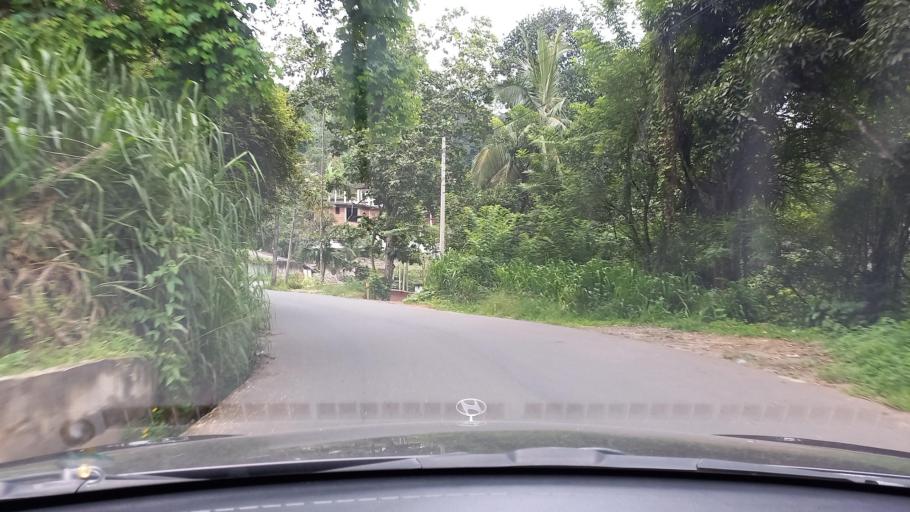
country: LK
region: Central
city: Kandy
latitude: 7.2323
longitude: 80.6053
